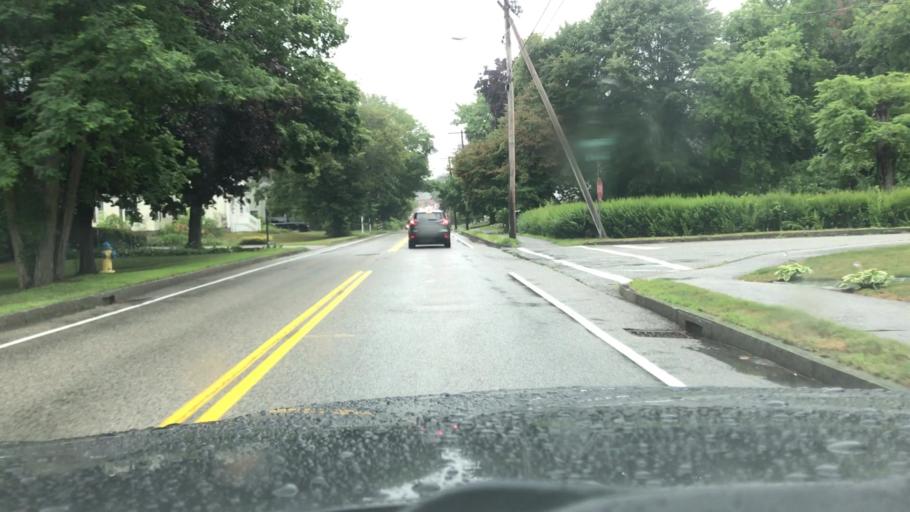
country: US
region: Maine
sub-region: York County
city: Kennebunk
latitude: 43.3892
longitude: -70.5421
